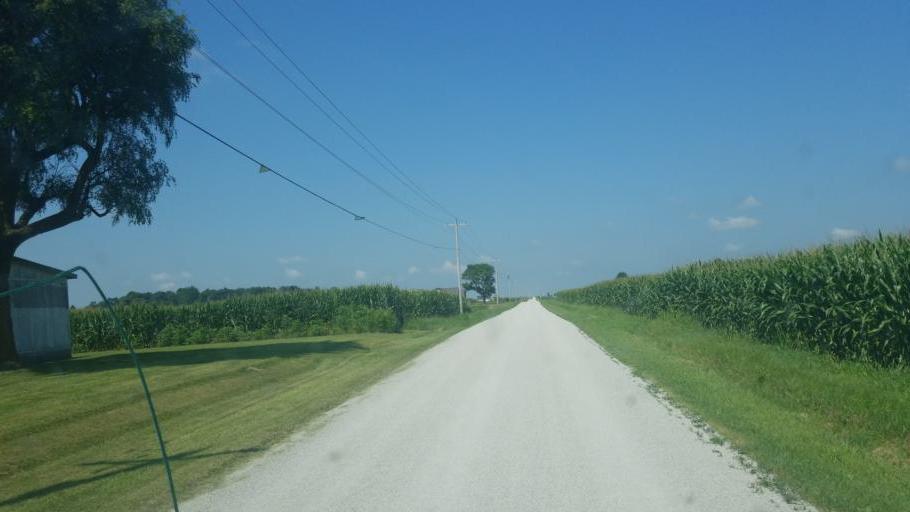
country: US
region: Ohio
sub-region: Hardin County
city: Kenton
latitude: 40.7033
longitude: -83.6798
